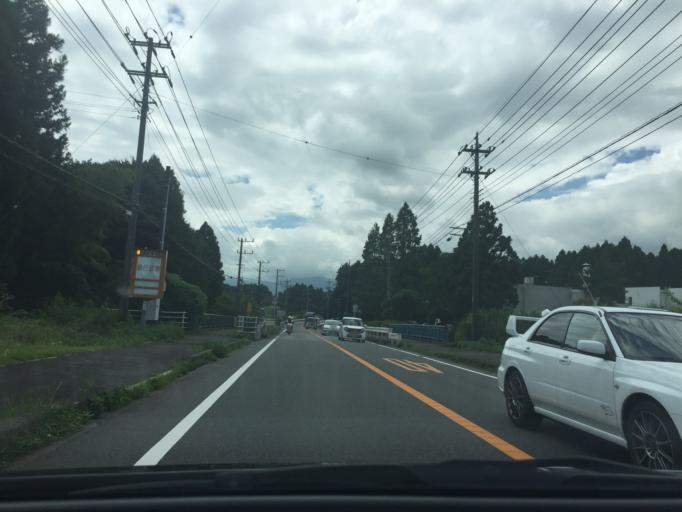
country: JP
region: Shizuoka
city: Gotemba
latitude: 35.2875
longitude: 138.8881
